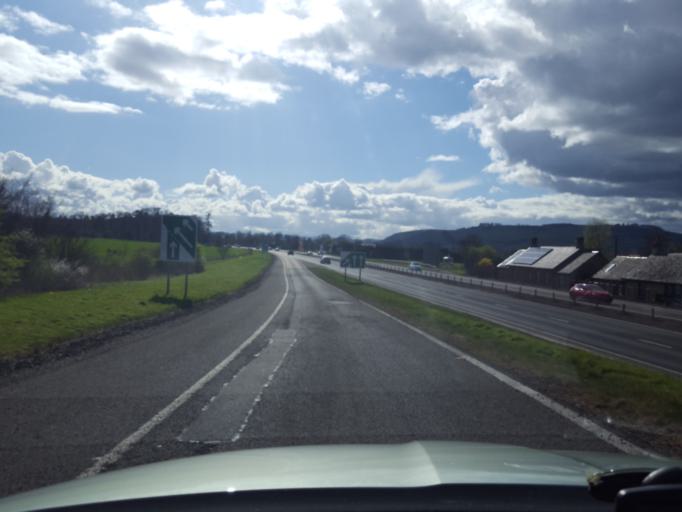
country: GB
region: Scotland
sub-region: Perth and Kinross
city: Errol
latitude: 56.4182
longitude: -3.2319
